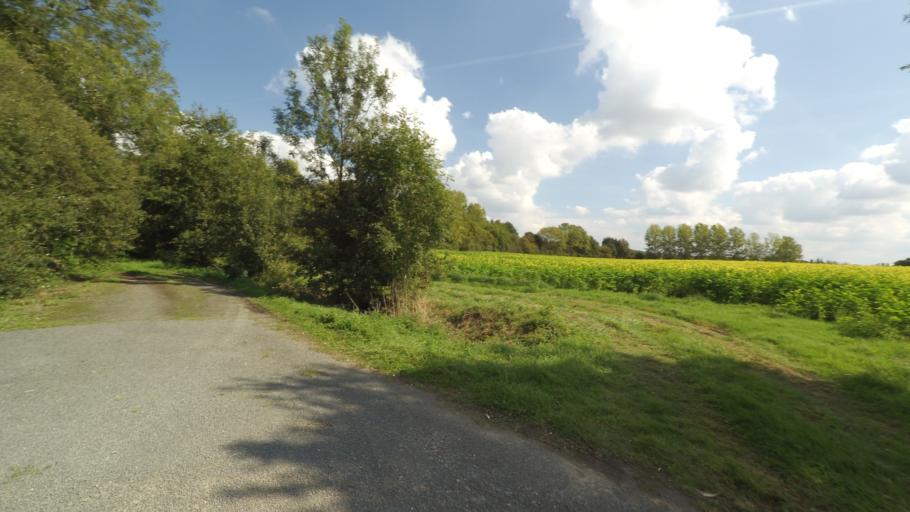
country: FR
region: Pays de la Loire
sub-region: Departement de la Vendee
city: Bouffere
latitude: 46.9603
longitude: -1.3660
